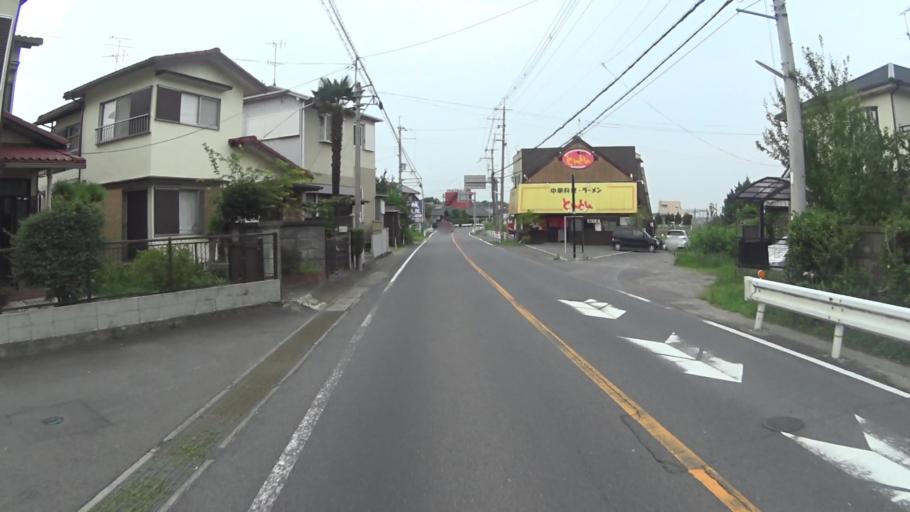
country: JP
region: Kyoto
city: Tanabe
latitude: 34.7837
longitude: 135.7877
